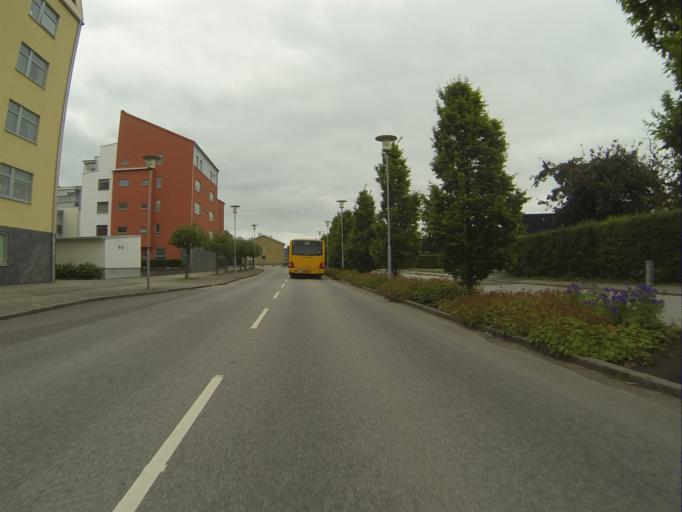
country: SE
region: Skane
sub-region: Staffanstorps Kommun
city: Staffanstorp
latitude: 55.6446
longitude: 13.2093
